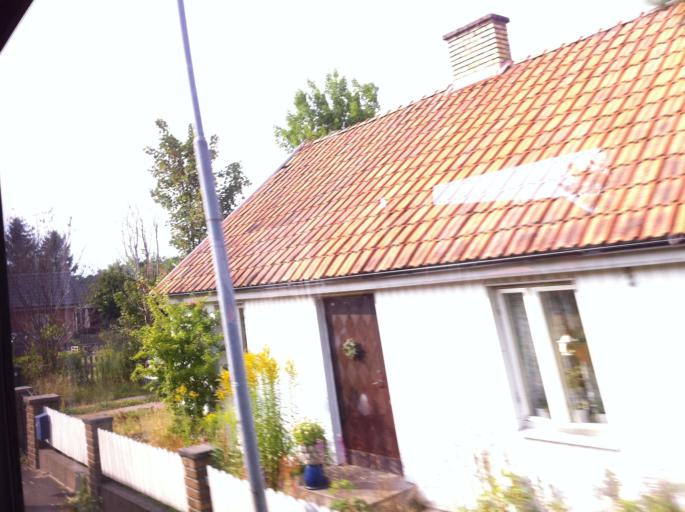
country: SE
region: Skane
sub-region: Kristianstads Kommun
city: Degeberga
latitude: 55.9000
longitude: 14.0823
